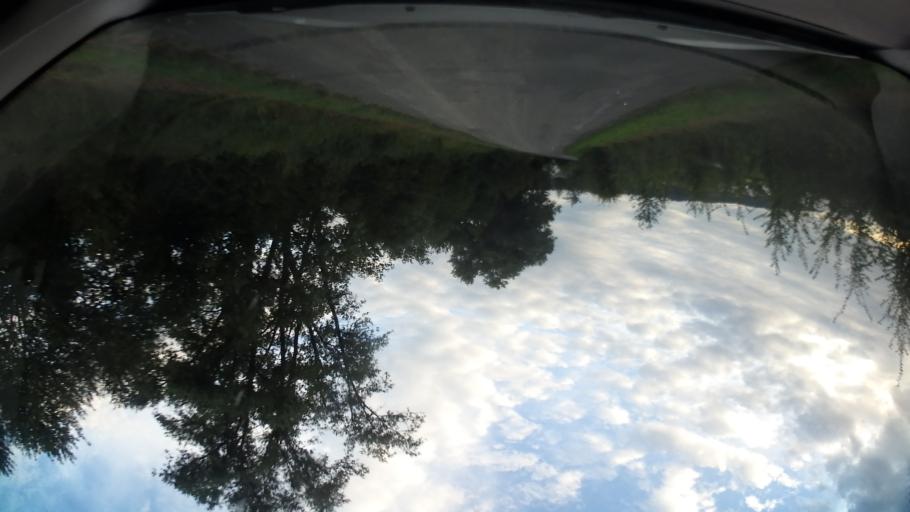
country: CZ
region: Olomoucky
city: Paseka
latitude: 49.8144
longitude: 17.2028
